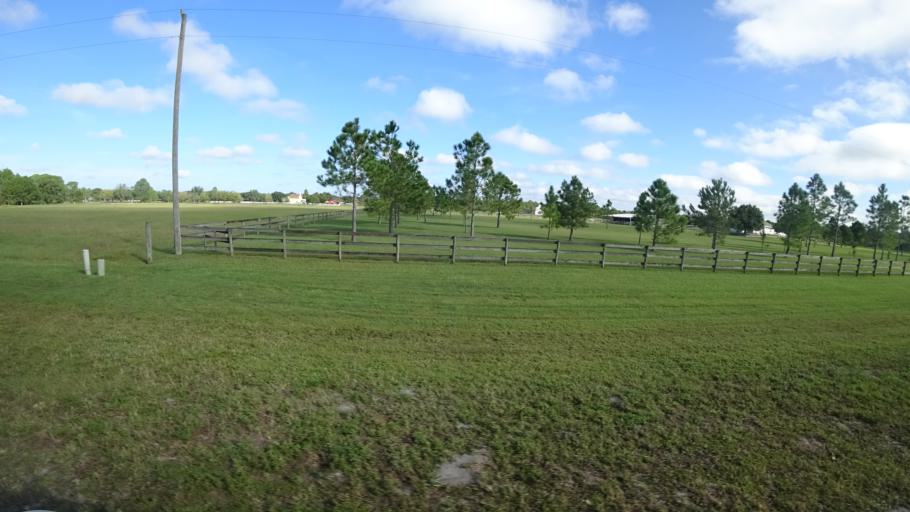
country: US
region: Florida
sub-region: Sarasota County
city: The Meadows
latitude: 27.4204
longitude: -82.3304
